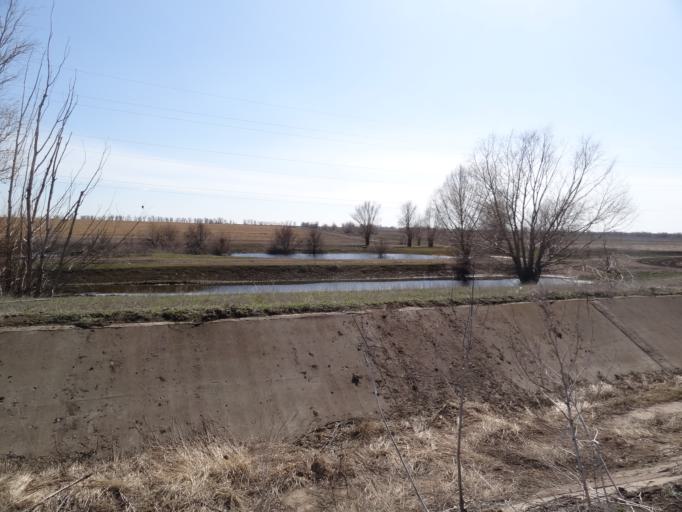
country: RU
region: Saratov
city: Engel's
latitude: 51.4028
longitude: 46.2246
